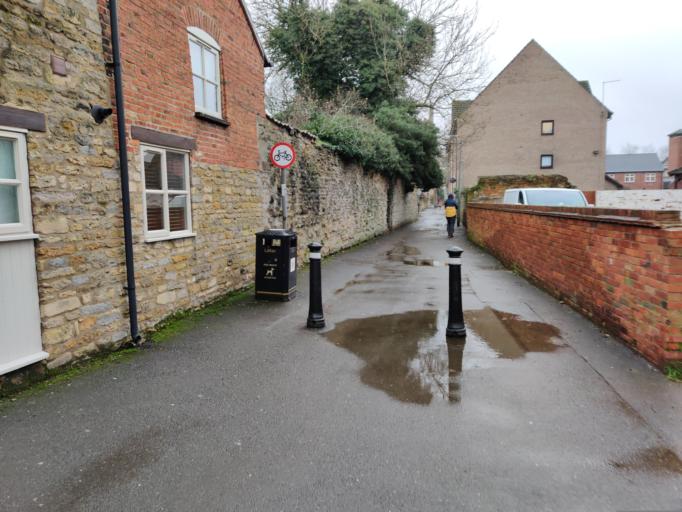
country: GB
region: England
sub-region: Lincolnshire
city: Bourne
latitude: 52.7676
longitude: -0.3762
